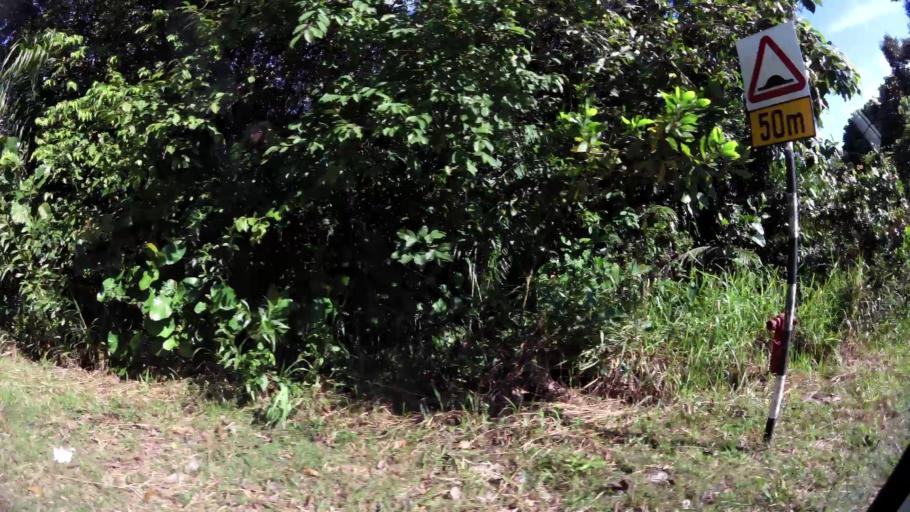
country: BN
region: Brunei and Muara
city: Bandar Seri Begawan
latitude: 4.9663
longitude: 114.9297
